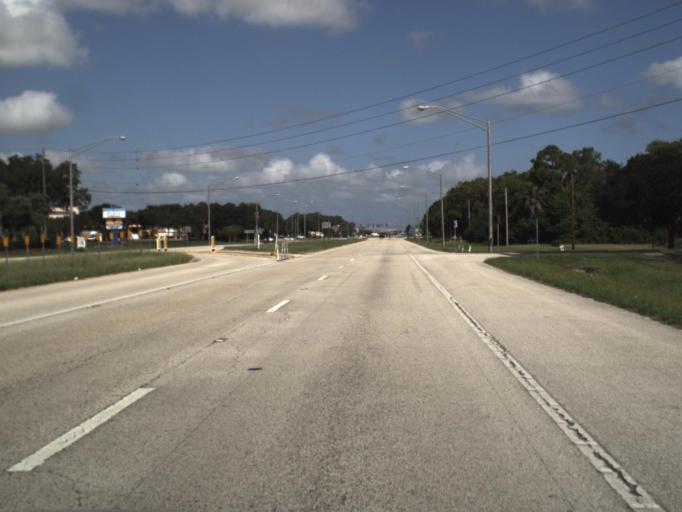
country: US
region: Florida
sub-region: Pinellas County
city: Gandy
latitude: 27.8672
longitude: -82.6432
